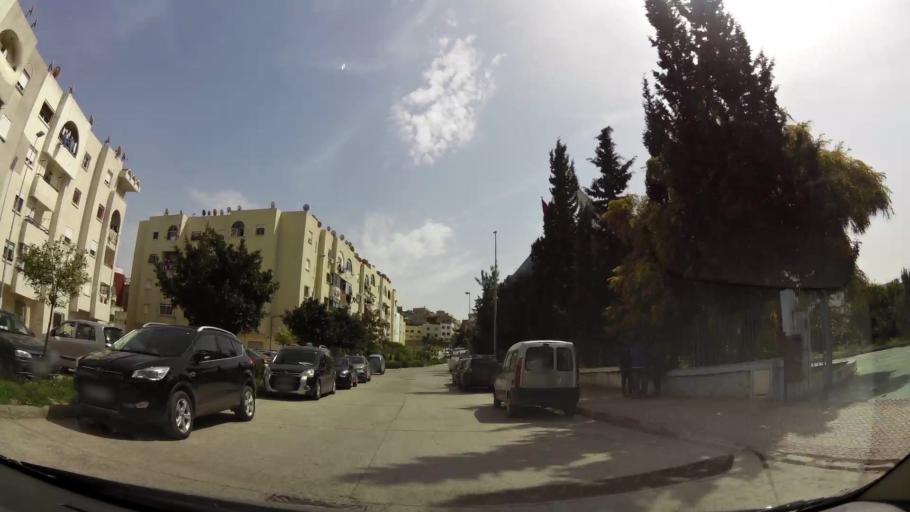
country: MA
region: Tanger-Tetouan
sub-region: Tanger-Assilah
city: Tangier
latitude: 35.7494
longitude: -5.8340
